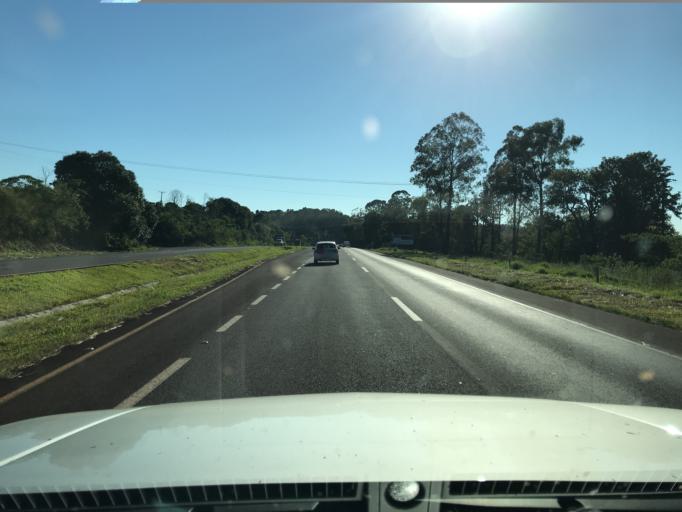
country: BR
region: Parana
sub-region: Cascavel
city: Cascavel
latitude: -24.8934
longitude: -53.5446
